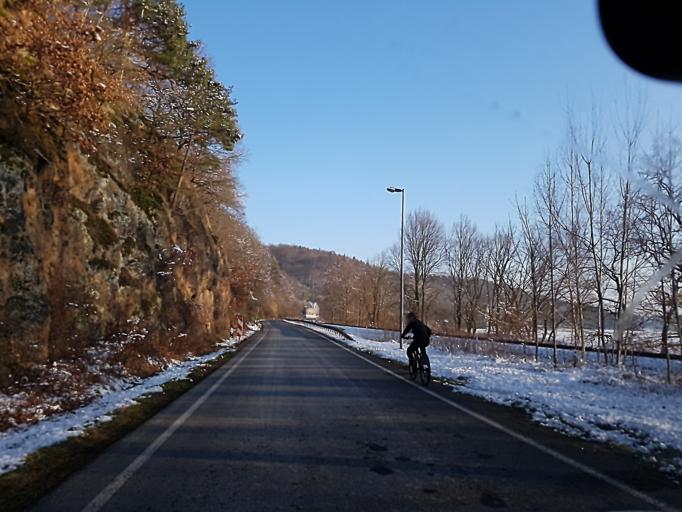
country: DE
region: Saxony
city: Grossweitzschen
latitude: 51.1575
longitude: 13.0058
